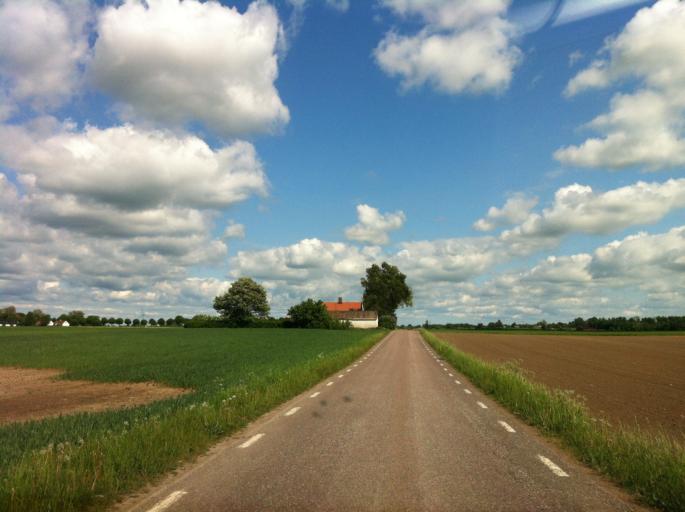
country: SE
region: Skane
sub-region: Landskrona
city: Asmundtorp
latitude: 55.9573
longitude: 12.9085
